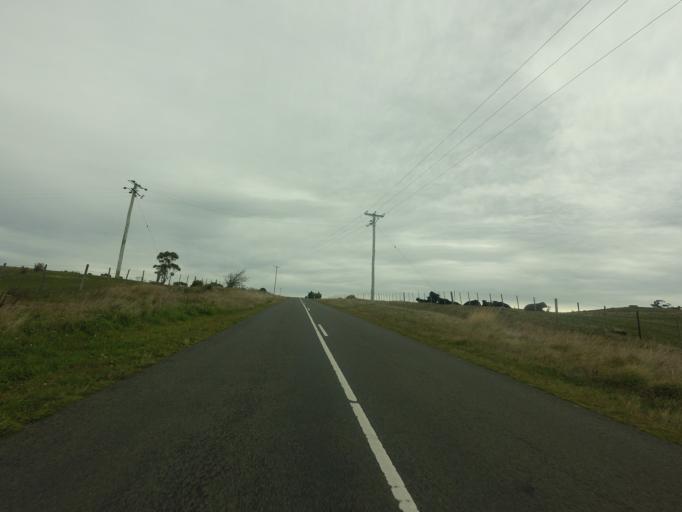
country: AU
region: Tasmania
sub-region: Derwent Valley
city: New Norfolk
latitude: -42.4051
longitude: 147.0081
